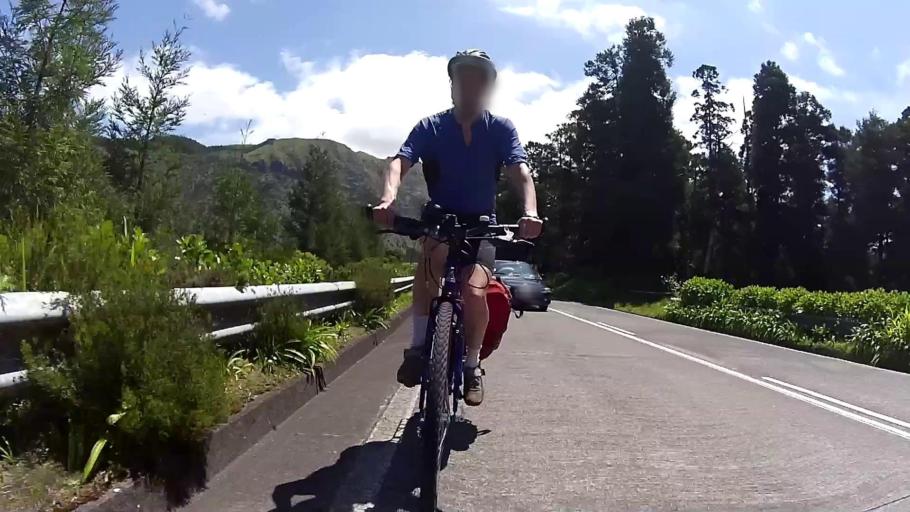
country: PT
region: Azores
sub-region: Ponta Delgada
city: Arrifes
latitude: 37.8537
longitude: -25.7730
